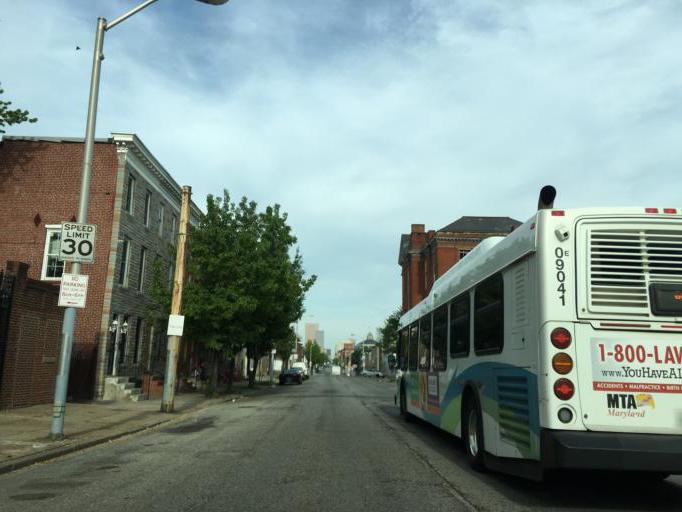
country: US
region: Maryland
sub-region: City of Baltimore
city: Baltimore
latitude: 39.2854
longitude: -76.6406
